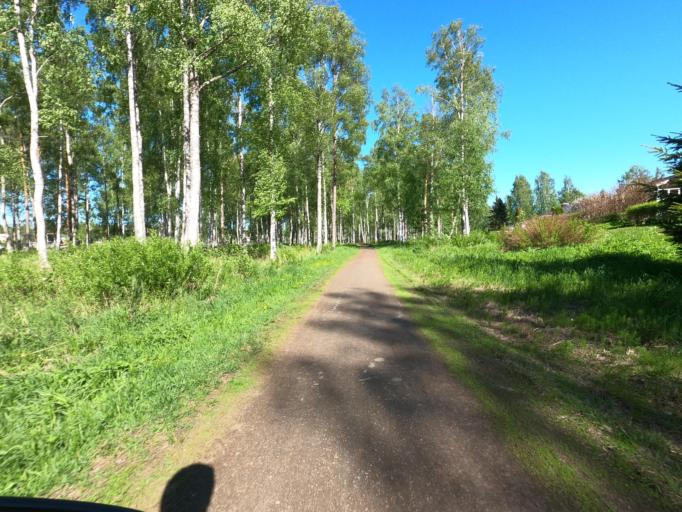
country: FI
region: North Karelia
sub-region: Joensuu
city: Joensuu
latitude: 62.6076
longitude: 29.7998
